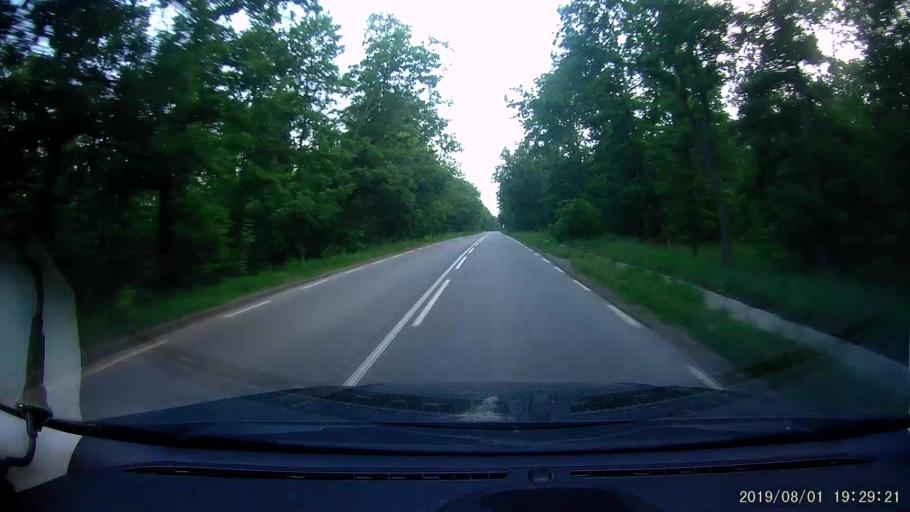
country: BG
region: Burgas
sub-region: Obshtina Sungurlare
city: Sungurlare
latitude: 42.8272
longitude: 26.9082
